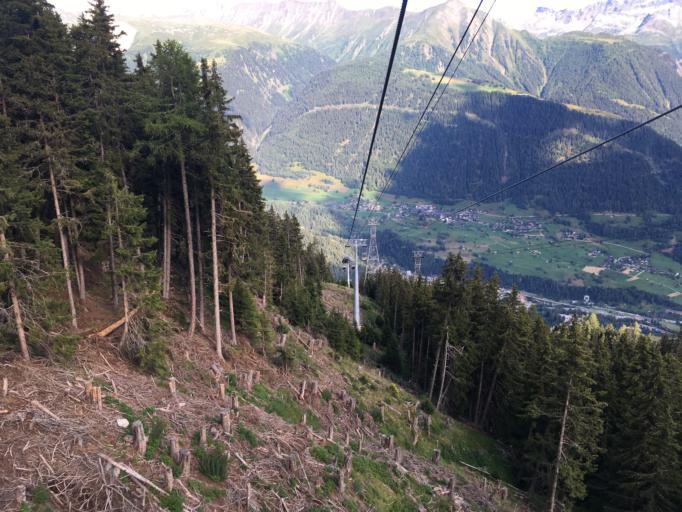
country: CH
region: Valais
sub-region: Goms District
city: Fiesch
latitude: 46.4116
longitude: 8.1106
